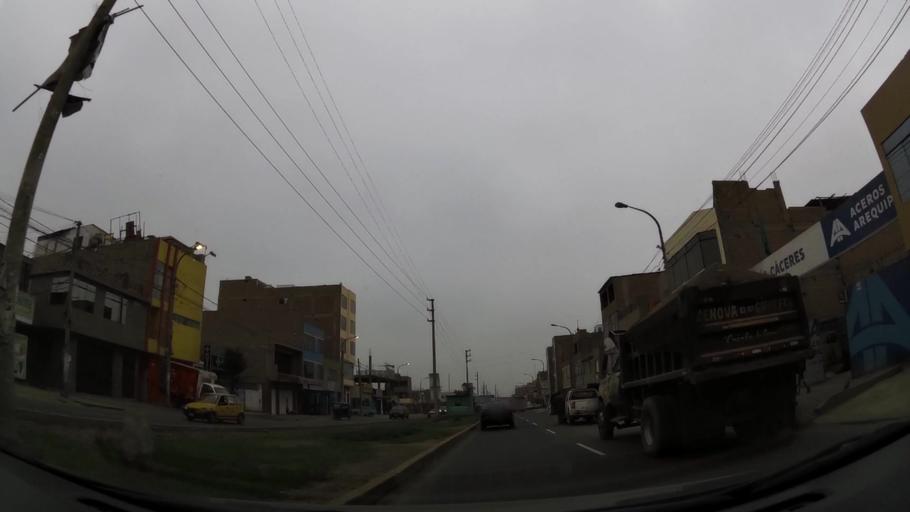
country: PE
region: Lima
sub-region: Lima
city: Urb. Santo Domingo
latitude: -11.8865
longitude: -77.0355
